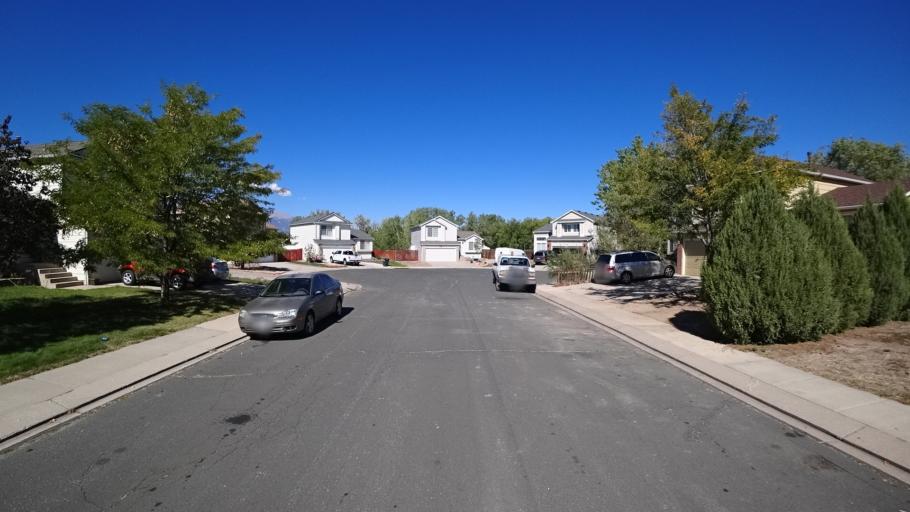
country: US
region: Colorado
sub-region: El Paso County
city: Stratmoor
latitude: 38.8137
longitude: -104.7430
